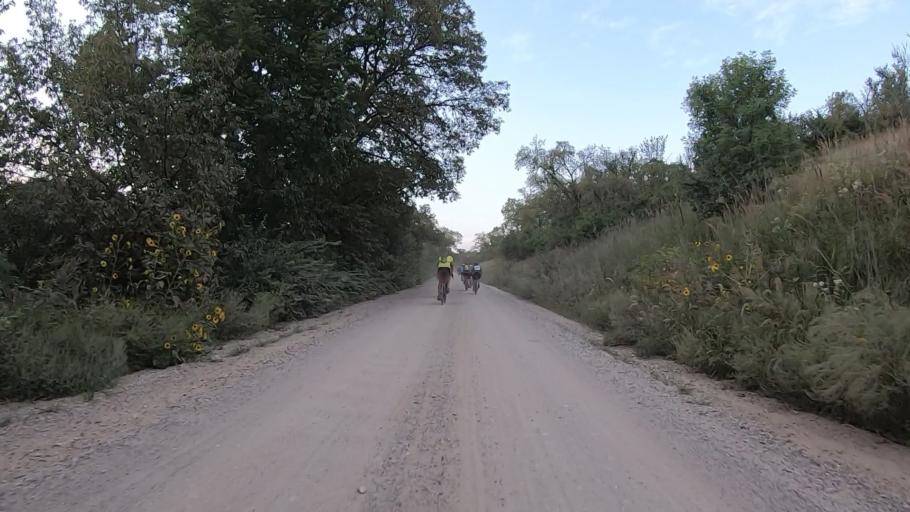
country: US
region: Kansas
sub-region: Marshall County
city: Marysville
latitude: 39.8352
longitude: -96.6655
